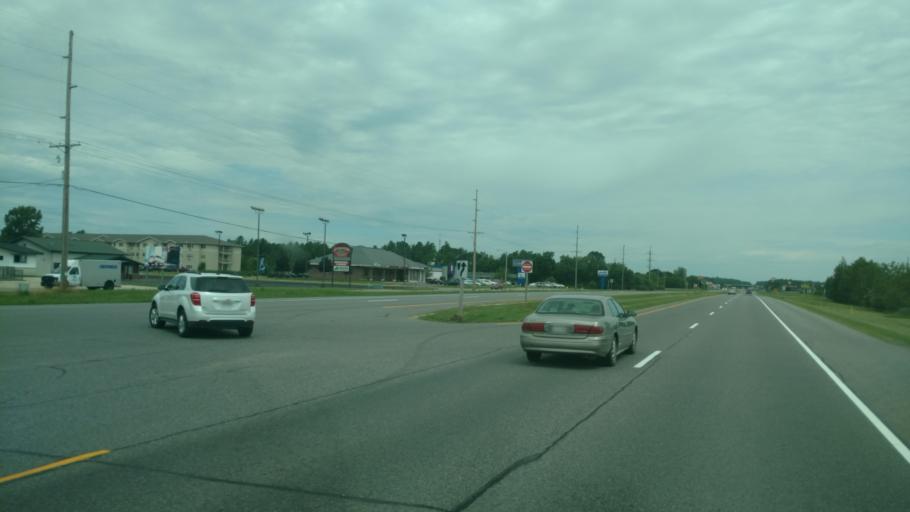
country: US
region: Wisconsin
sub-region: Monroe County
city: Tomah
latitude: 44.0080
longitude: -90.5049
